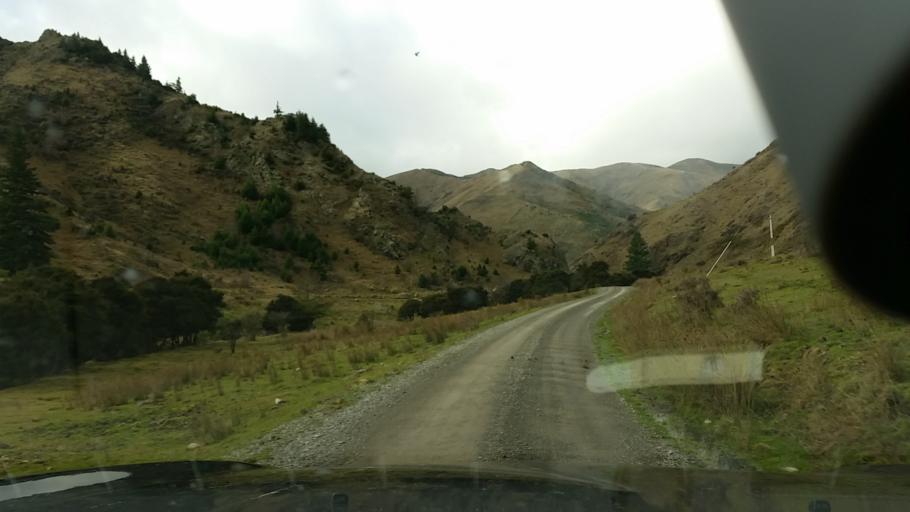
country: NZ
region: Tasman
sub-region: Tasman District
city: Richmond
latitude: -41.7311
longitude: 173.4549
